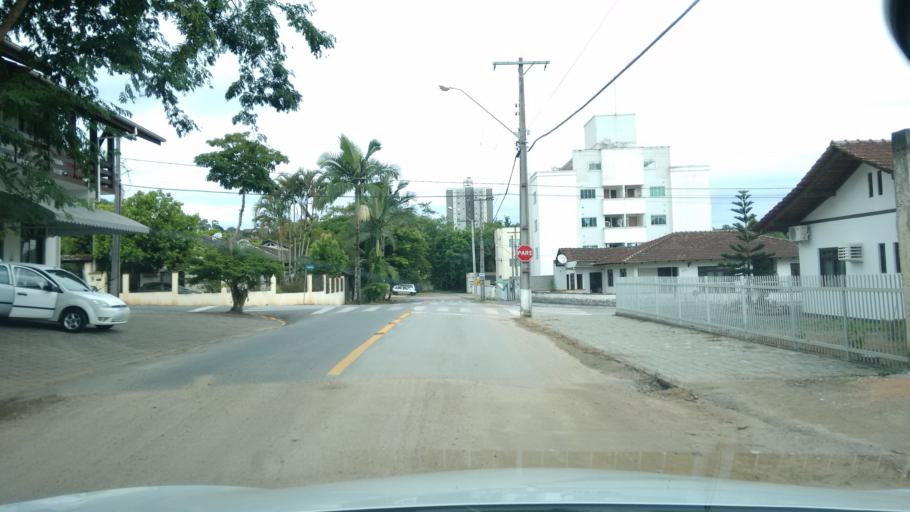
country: BR
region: Santa Catarina
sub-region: Timbo
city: Timbo
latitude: -26.8116
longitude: -49.2663
